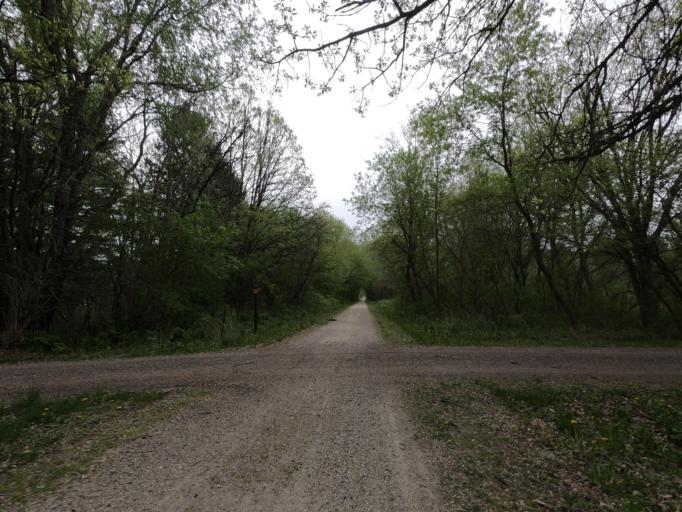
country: US
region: Wisconsin
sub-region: Jefferson County
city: Lake Mills
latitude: 43.0466
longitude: -88.8612
